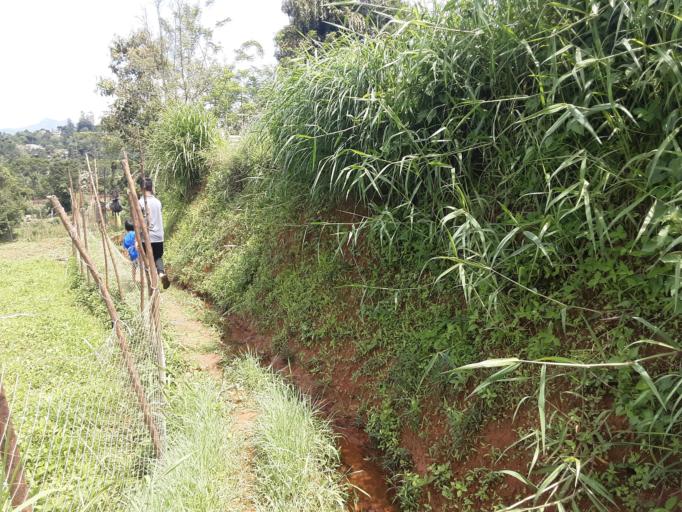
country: LK
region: Uva
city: Haputale
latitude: 6.8945
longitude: 80.9265
